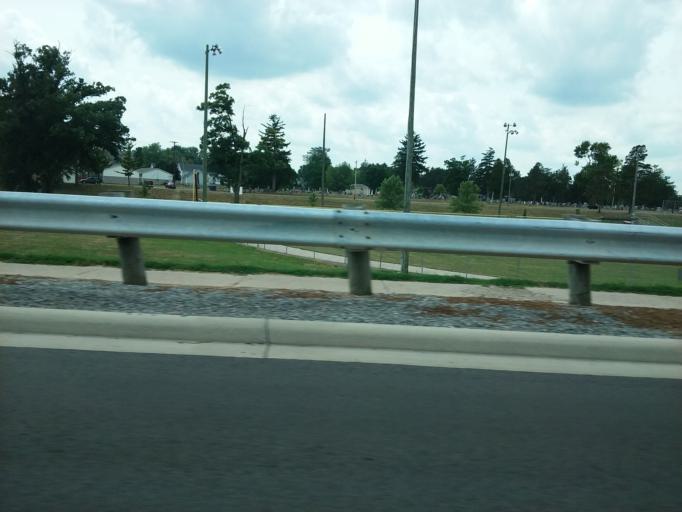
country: US
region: Ohio
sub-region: Hancock County
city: Findlay
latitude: 41.0454
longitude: -83.6616
